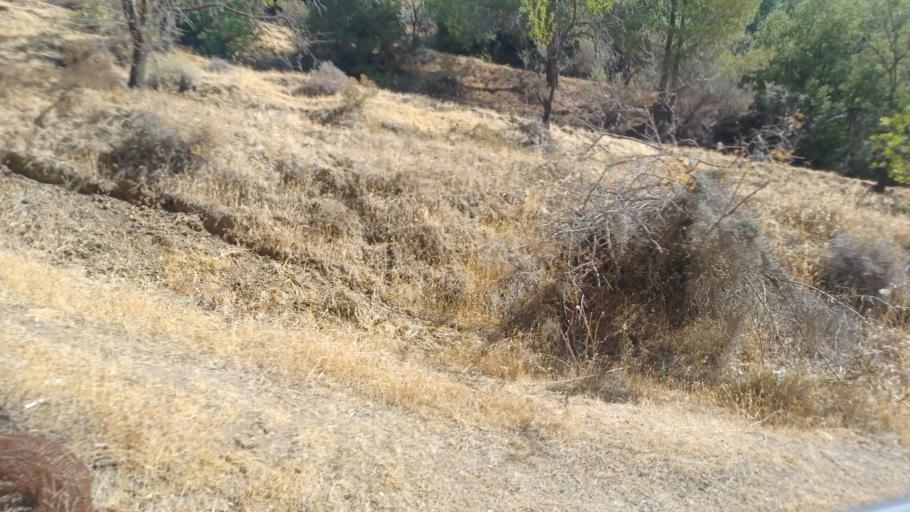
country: CY
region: Pafos
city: Mesogi
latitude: 34.9324
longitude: 32.6332
